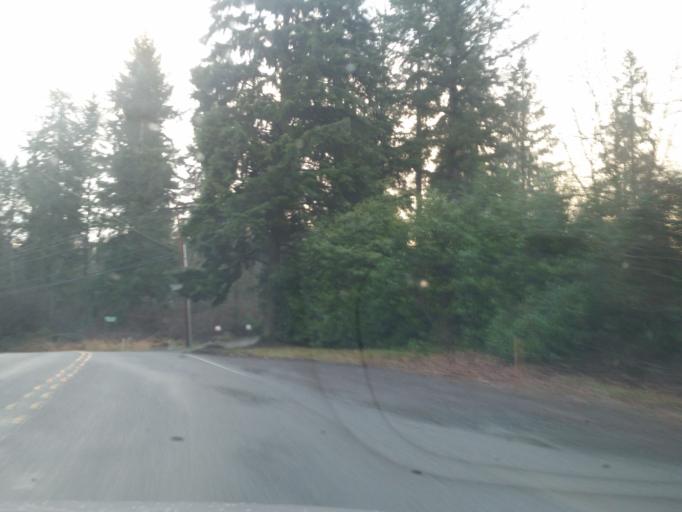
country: US
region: Washington
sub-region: Snohomish County
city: Maltby
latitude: 47.8156
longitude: -122.0927
